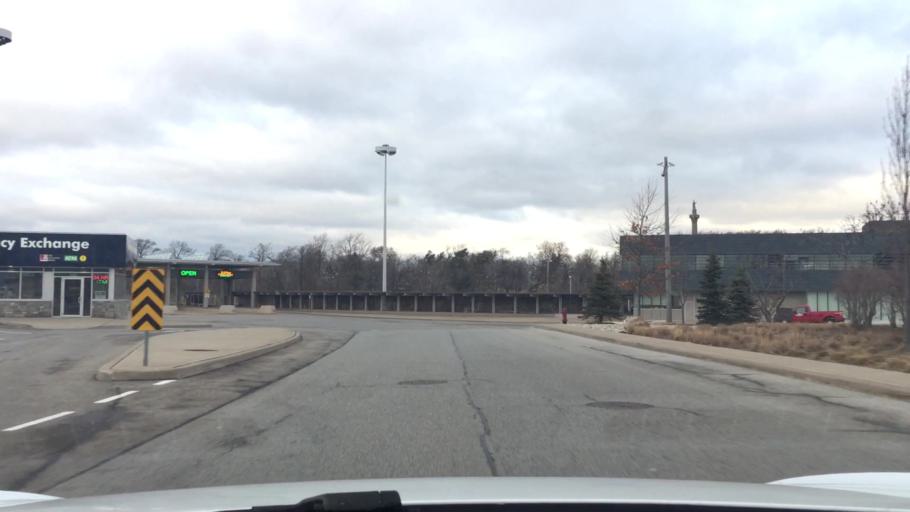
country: US
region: New York
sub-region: Niagara County
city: Lewiston
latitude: 43.1560
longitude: -79.0511
